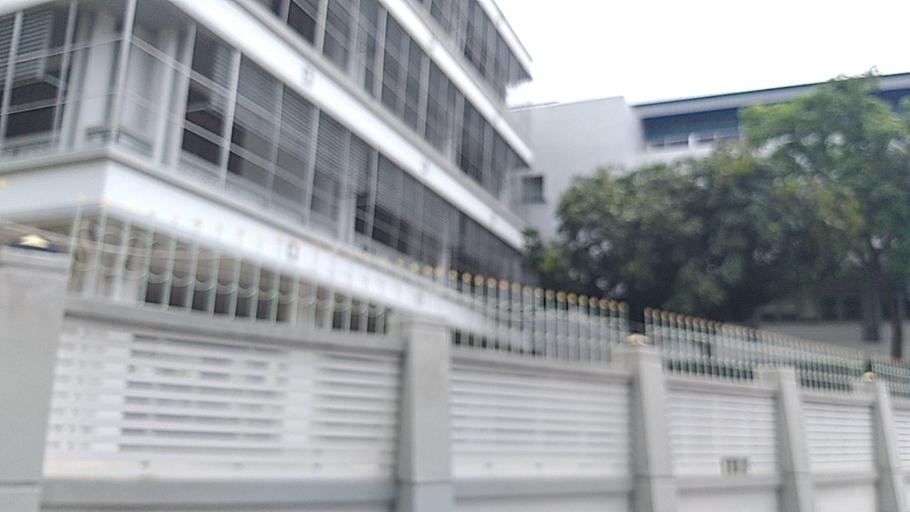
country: TH
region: Nakhon Pathom
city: Nakhon Pathom
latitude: 13.8212
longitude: 100.0562
